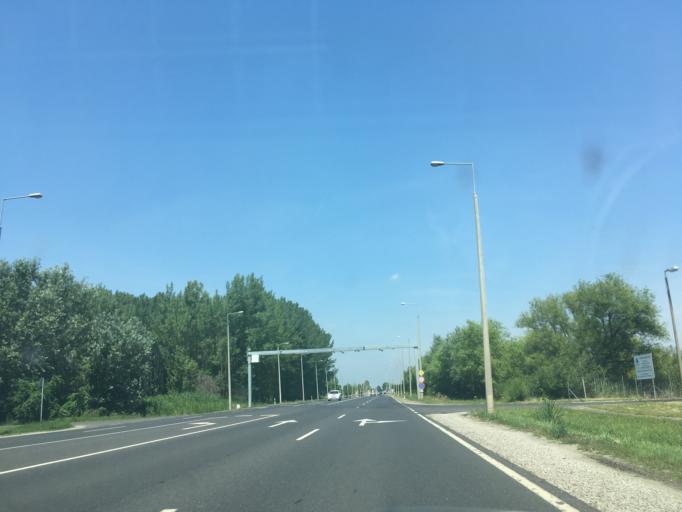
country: HU
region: Hajdu-Bihar
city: Mikepercs
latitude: 47.4884
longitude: 21.6329
